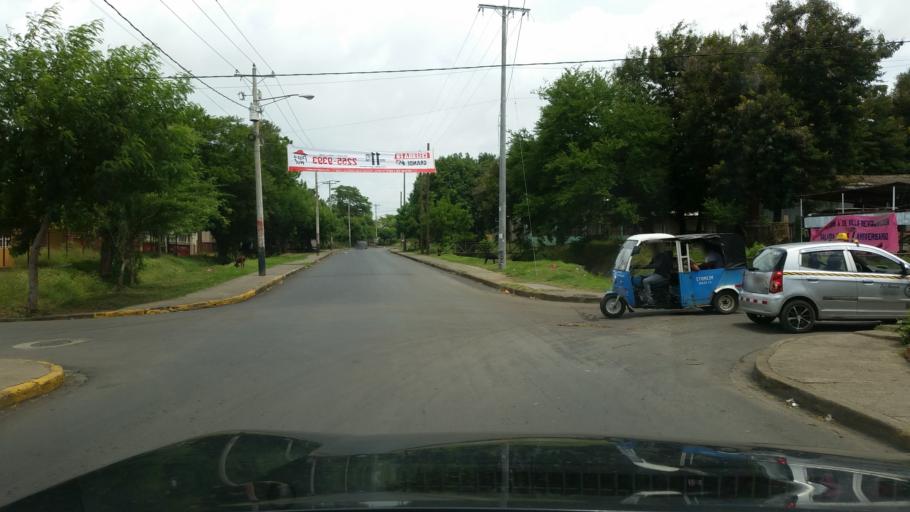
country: NI
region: Managua
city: Managua
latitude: 12.1313
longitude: -86.2129
